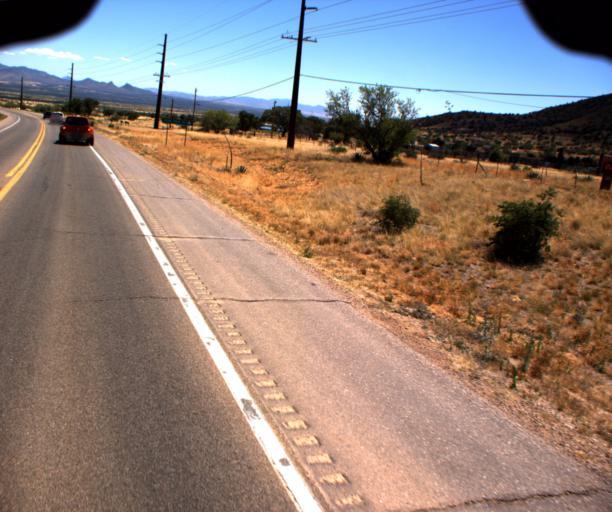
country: US
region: Arizona
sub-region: Cochise County
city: Sierra Vista Southeast
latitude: 31.3841
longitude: -110.2249
